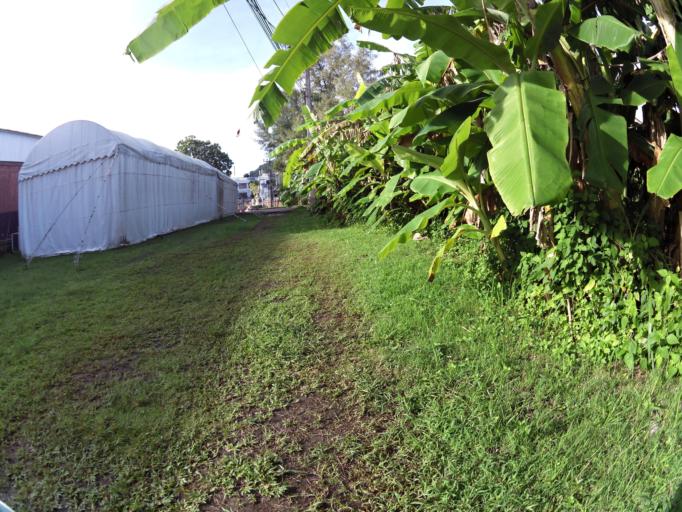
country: TH
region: Phuket
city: Patong
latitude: 7.9482
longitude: 98.2801
